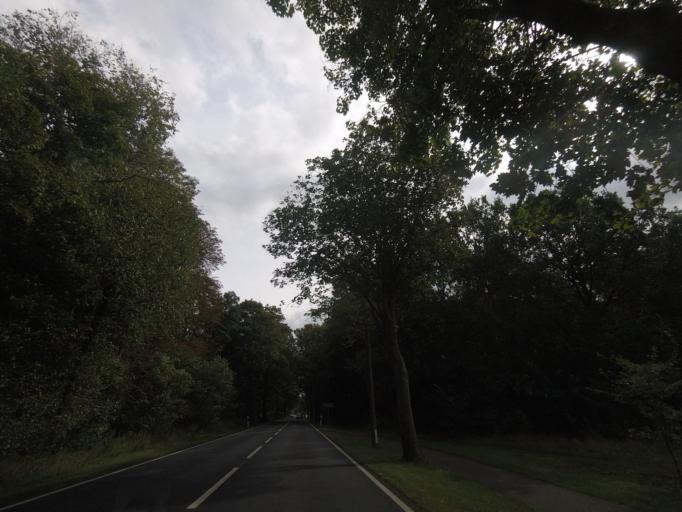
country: DE
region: Brandenburg
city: Niedergorsdorf
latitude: 52.0064
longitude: 13.0163
